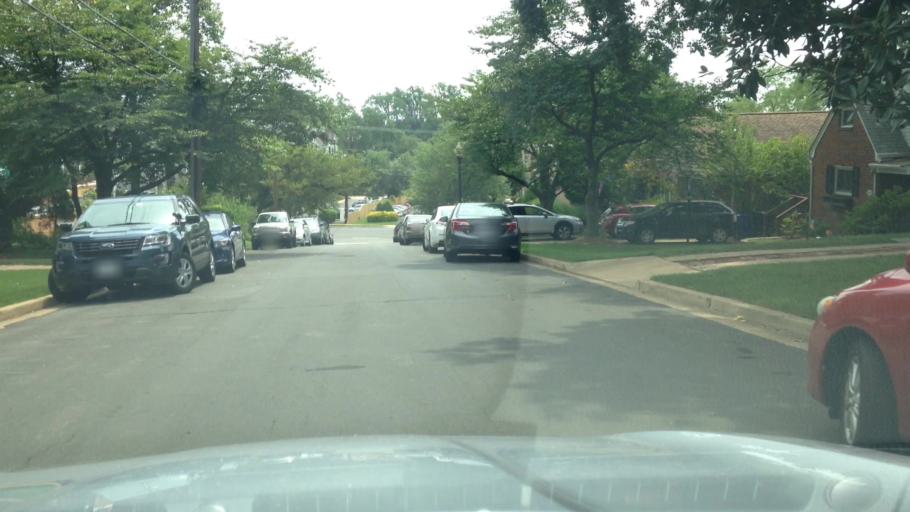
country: US
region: Virginia
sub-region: Fairfax County
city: Seven Corners
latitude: 38.8965
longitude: -77.1411
